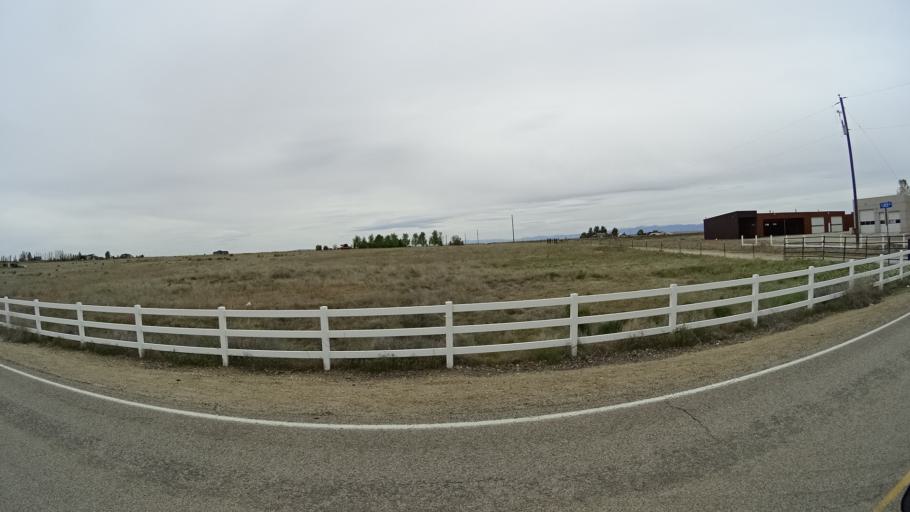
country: US
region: Idaho
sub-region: Ada County
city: Kuna
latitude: 43.4884
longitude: -116.3040
